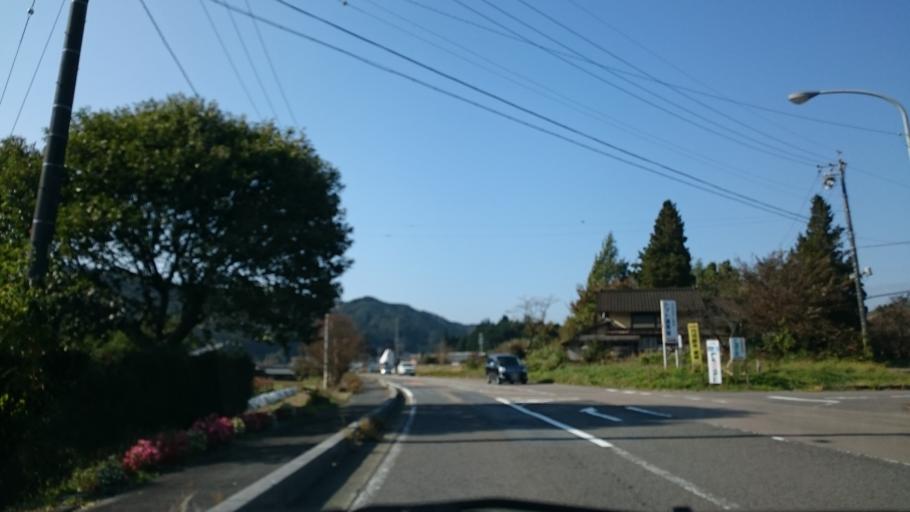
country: JP
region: Gifu
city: Nakatsugawa
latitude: 35.7432
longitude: 137.3390
